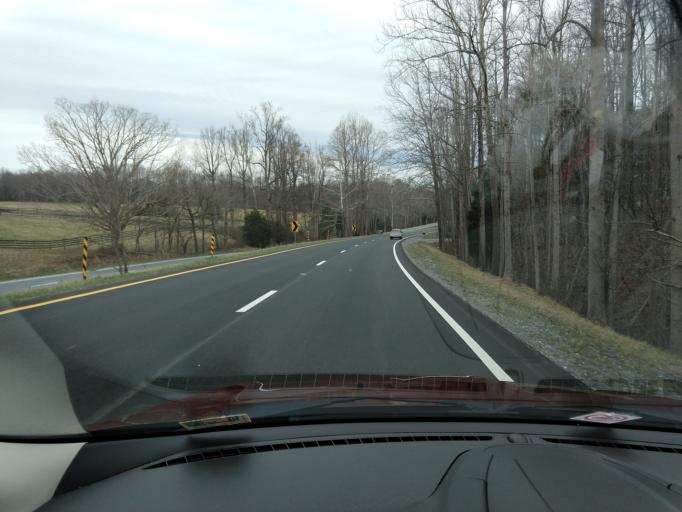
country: US
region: Virginia
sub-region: Franklin County
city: Henry Fork
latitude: 36.8576
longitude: -79.8739
